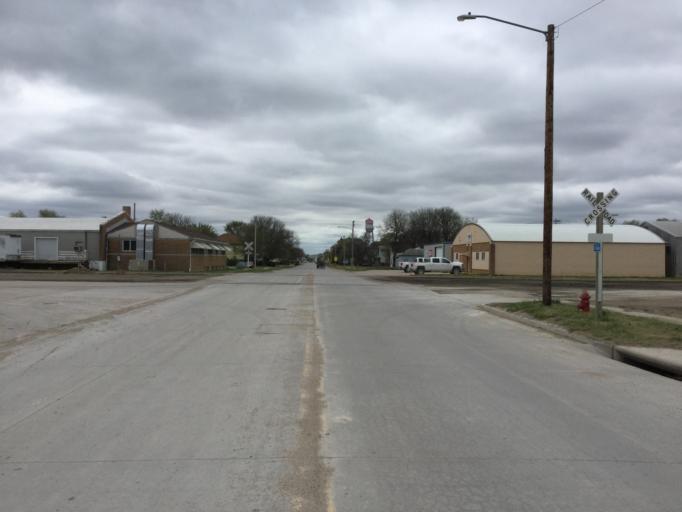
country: US
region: Kansas
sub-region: Osborne County
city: Osborne
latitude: 39.4438
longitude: -98.6948
